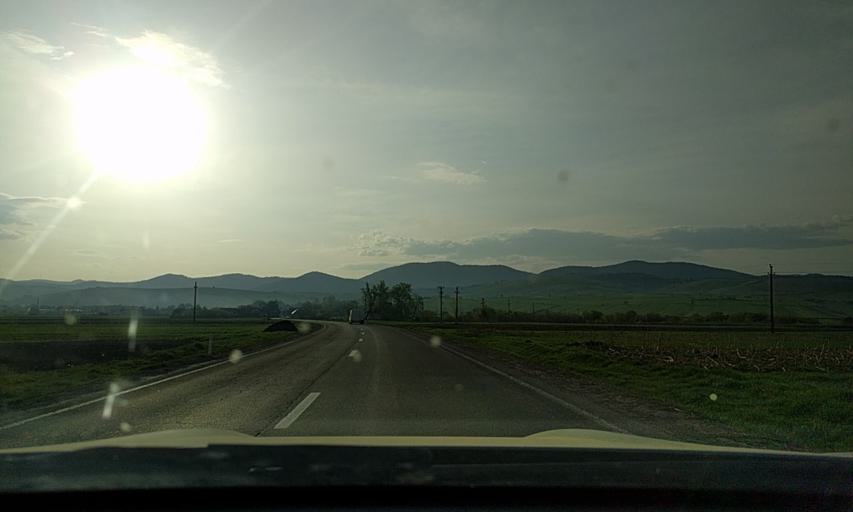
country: RO
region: Covasna
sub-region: Comuna Lemnia
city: Lemnia
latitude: 46.0427
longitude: 26.2820
